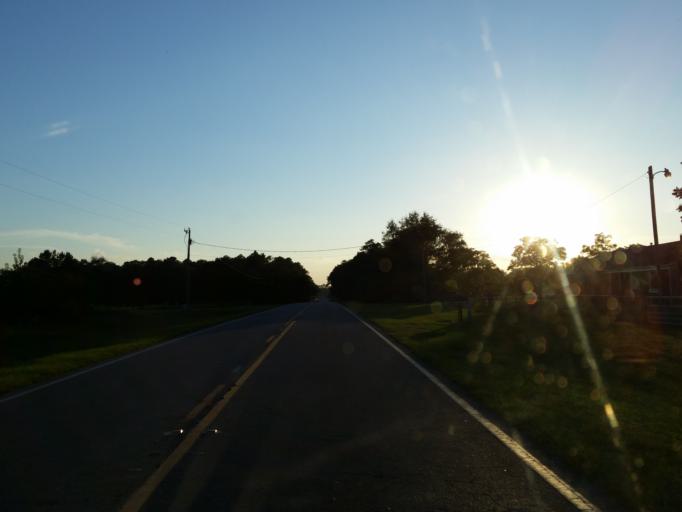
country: US
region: Georgia
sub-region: Berrien County
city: Nashville
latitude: 31.1862
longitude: -83.1718
